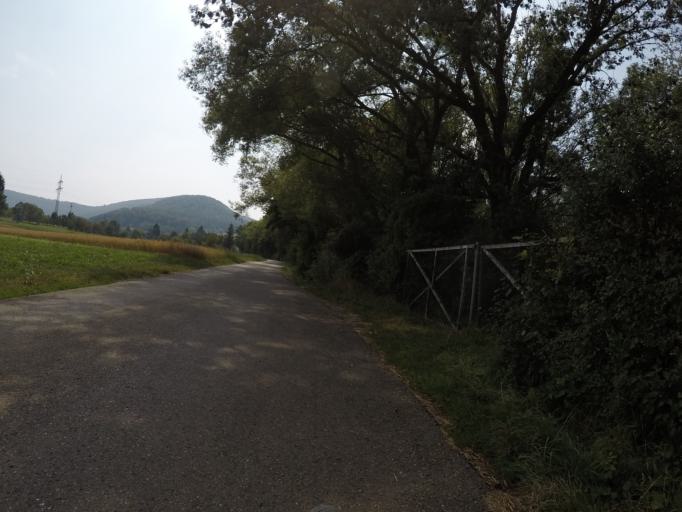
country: DE
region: Baden-Wuerttemberg
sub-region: Tuebingen Region
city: Pfullingen
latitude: 48.4523
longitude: 9.2087
